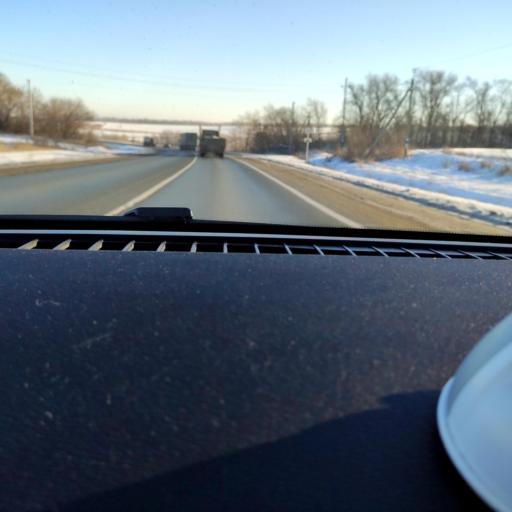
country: RU
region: Samara
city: Smyshlyayevka
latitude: 53.1480
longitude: 50.5041
